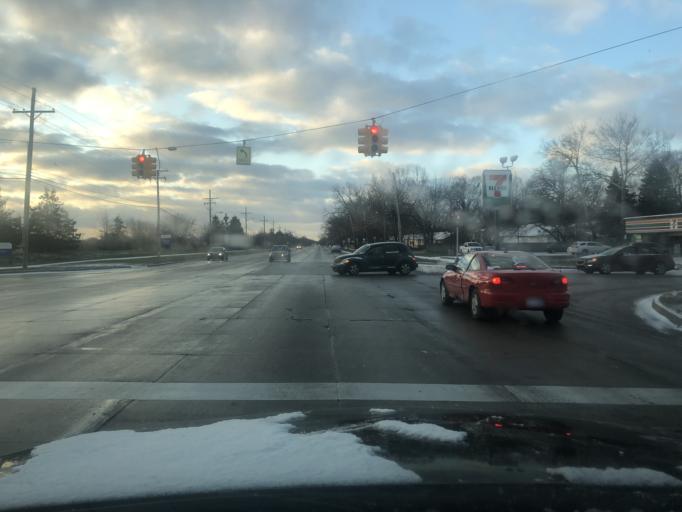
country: US
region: Michigan
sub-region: Wayne County
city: Garden City
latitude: 42.2967
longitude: -83.3493
